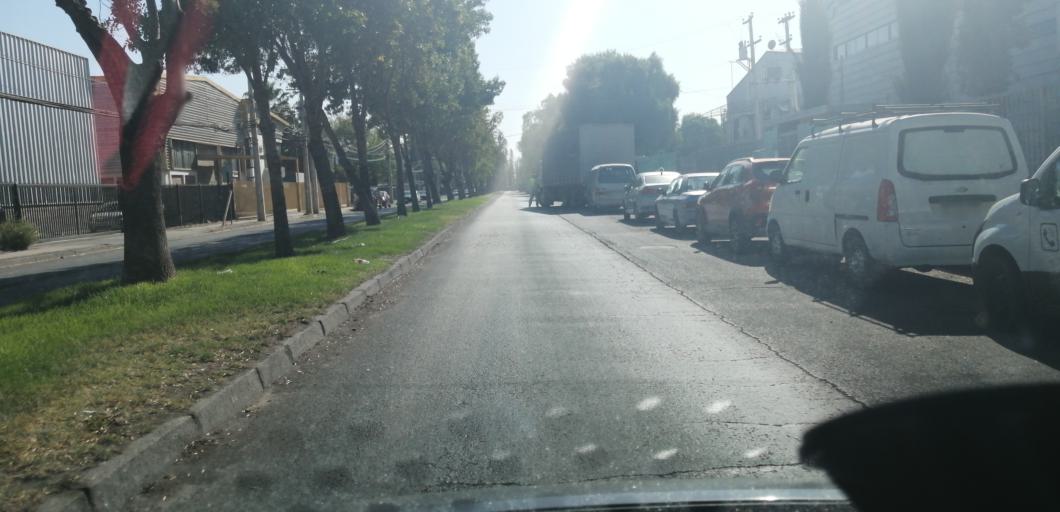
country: CL
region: Santiago Metropolitan
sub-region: Provincia de Santiago
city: Lo Prado
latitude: -33.3824
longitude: -70.7743
